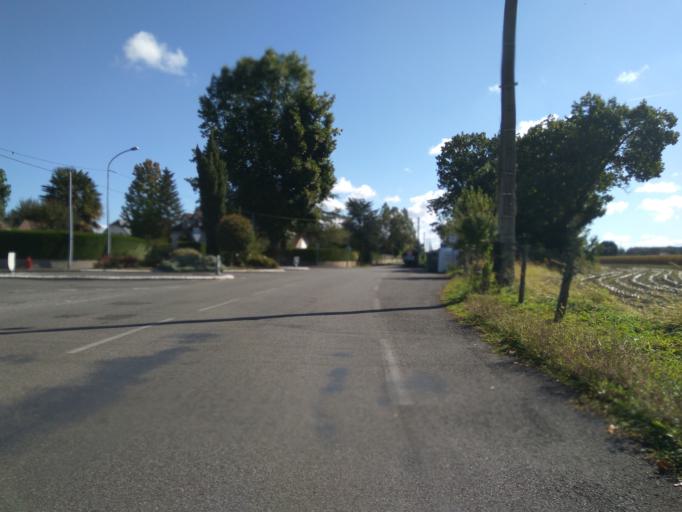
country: FR
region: Aquitaine
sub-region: Departement des Pyrenees-Atlantiques
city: Idron
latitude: 43.3022
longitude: -0.3252
